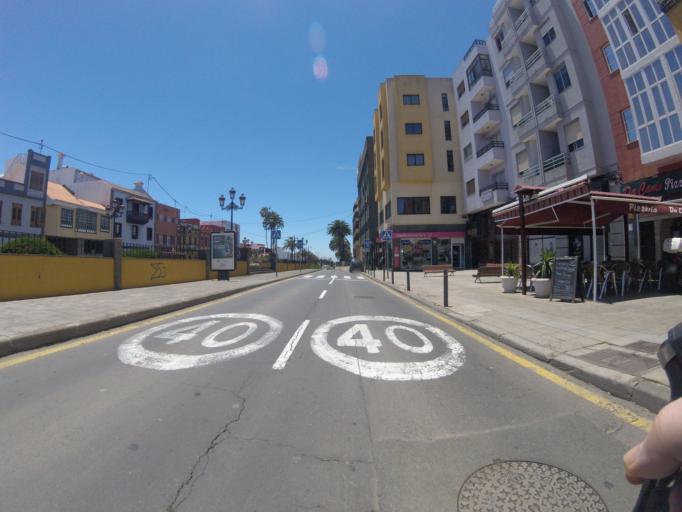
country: ES
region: Canary Islands
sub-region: Provincia de Santa Cruz de Tenerife
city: La Laguna
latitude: 28.4844
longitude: -16.3140
